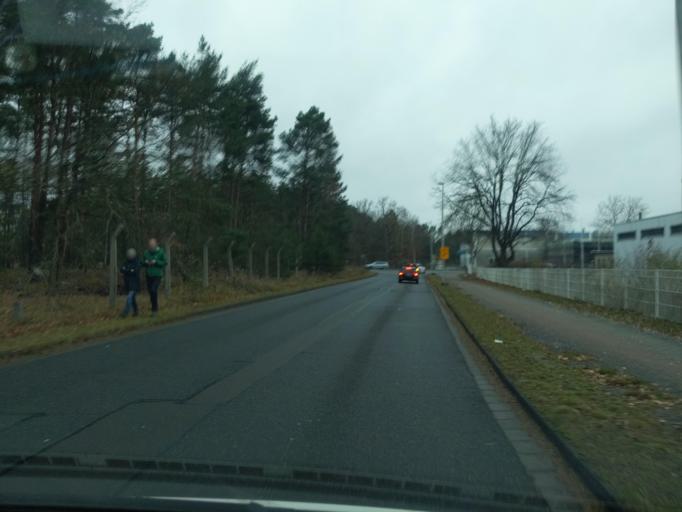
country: DE
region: Brandenburg
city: Cottbus
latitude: 51.7057
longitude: 14.3525
